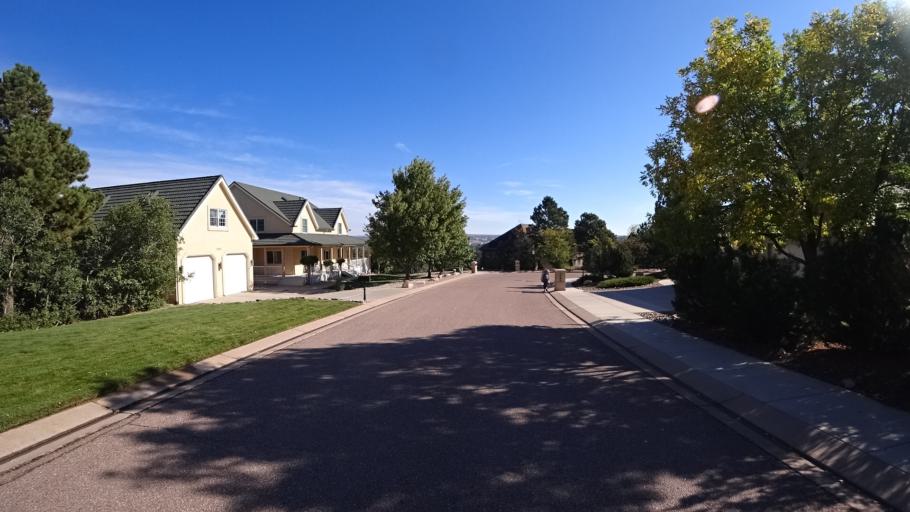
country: US
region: Colorado
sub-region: El Paso County
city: Colorado Springs
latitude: 38.9124
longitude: -104.8016
